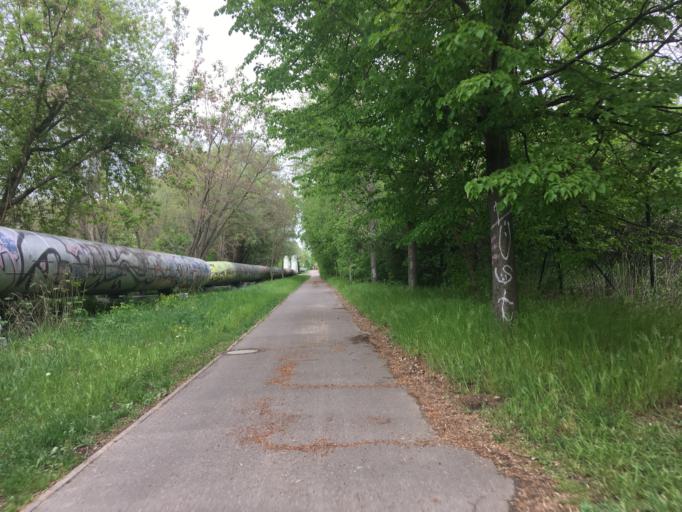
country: DE
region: Berlin
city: Falkenberg
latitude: 52.5496
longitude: 13.5308
